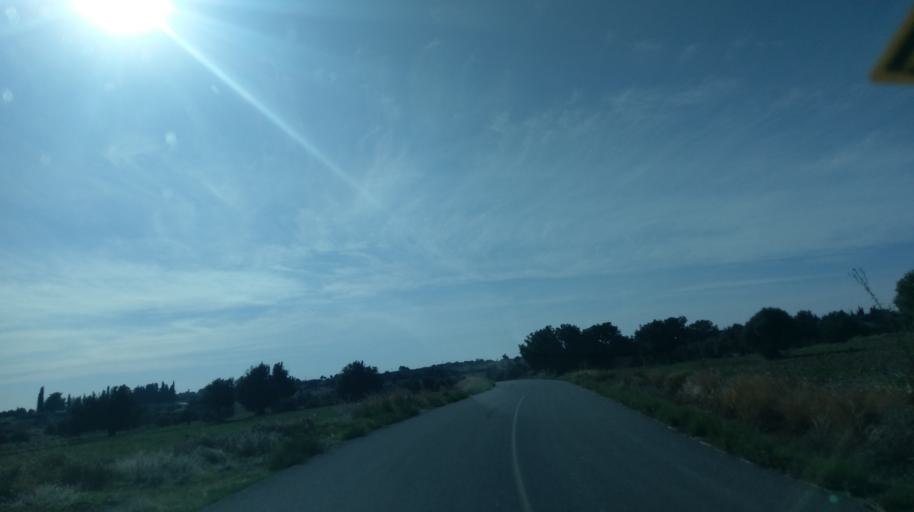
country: CY
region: Ammochostos
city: Trikomo
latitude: 35.3465
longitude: 33.8784
